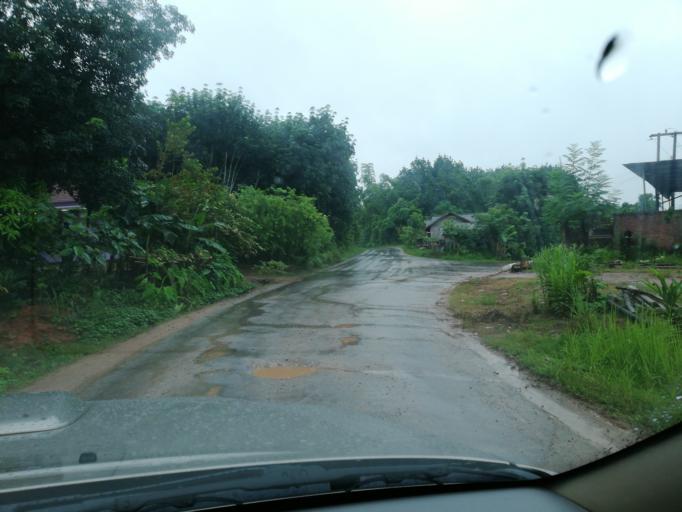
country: LA
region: Loungnamtha
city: Louang Namtha
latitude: 20.9987
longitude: 101.3980
